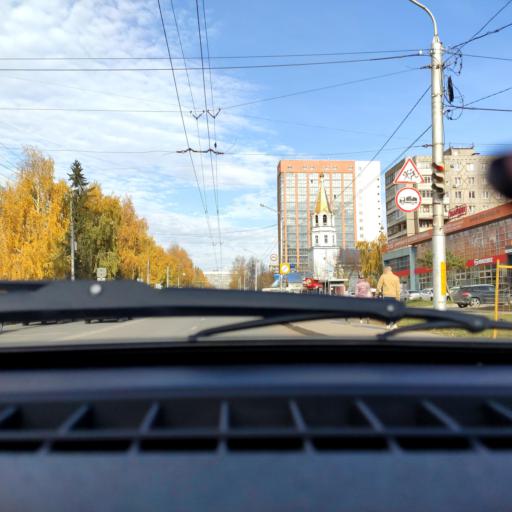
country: RU
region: Bashkortostan
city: Ufa
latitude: 54.7811
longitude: 56.1314
